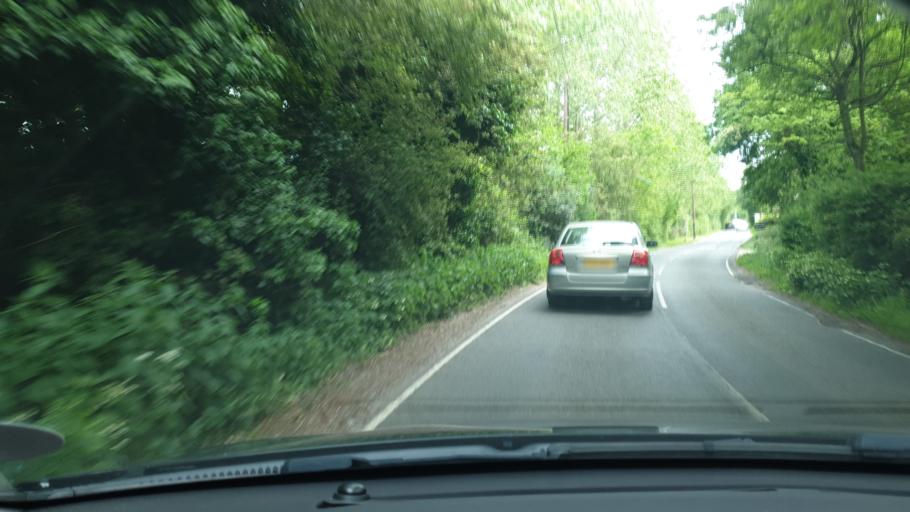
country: GB
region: England
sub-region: Essex
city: Great Bentley
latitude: 51.8634
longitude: 1.1006
